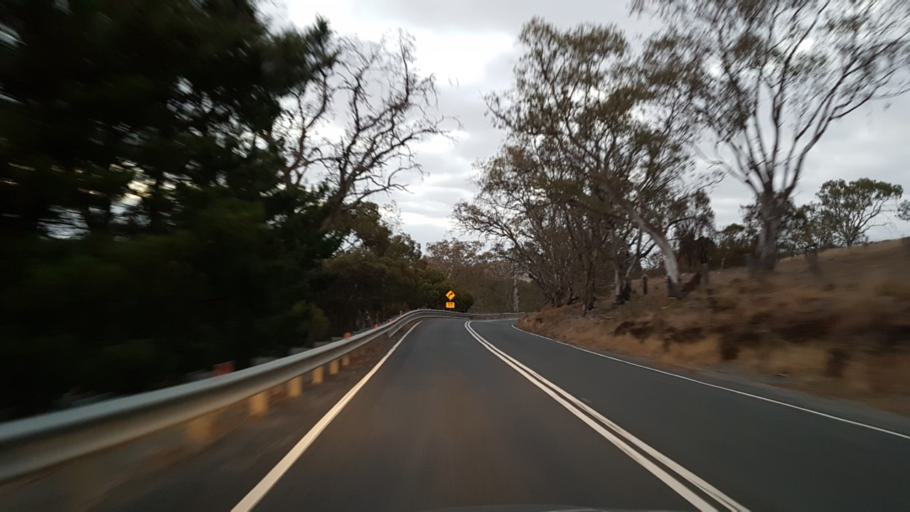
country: AU
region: South Australia
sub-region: Mount Barker
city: Nairne
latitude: -35.0317
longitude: 138.9652
